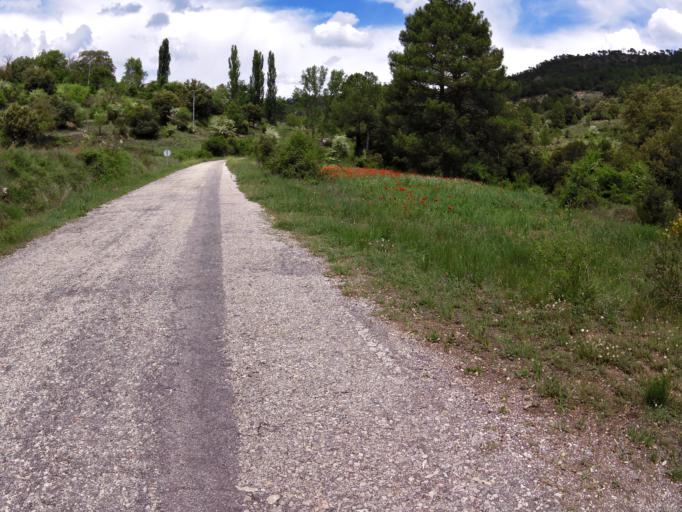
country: ES
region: Castille-La Mancha
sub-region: Provincia de Albacete
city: Paterna del Madera
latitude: 38.5759
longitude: -2.3375
